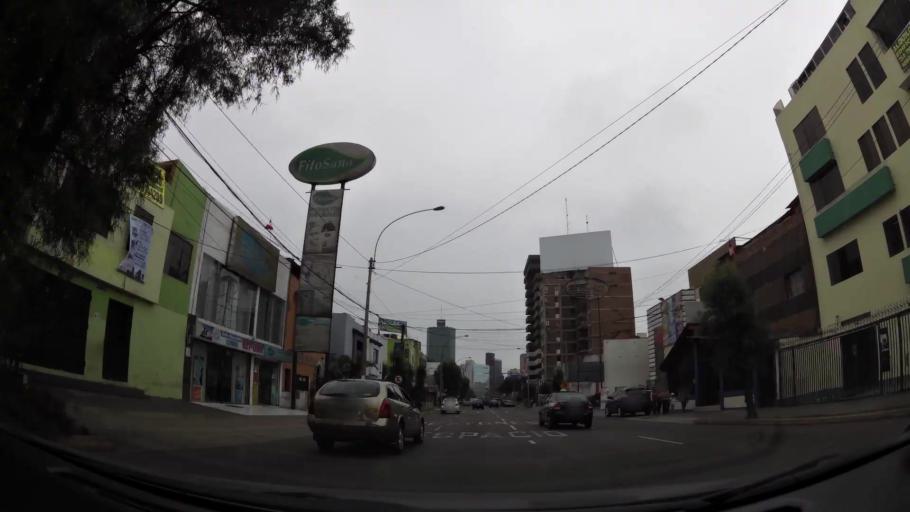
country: PE
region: Lima
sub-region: Lima
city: San Isidro
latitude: -12.0893
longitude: -77.0349
